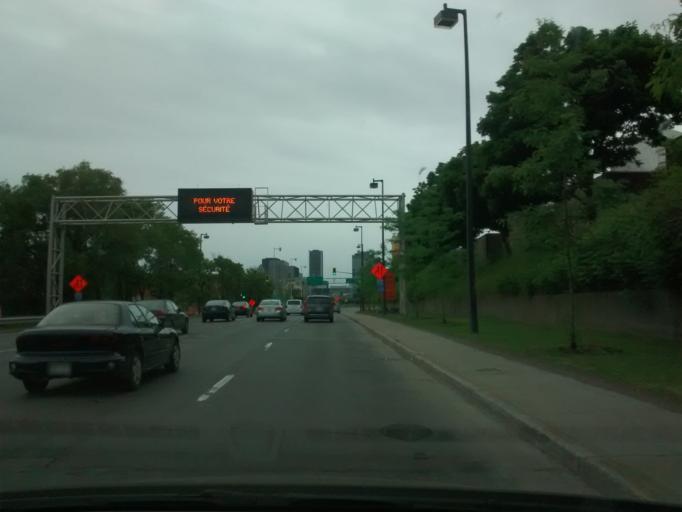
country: CA
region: Quebec
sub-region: Monteregie
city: Longueuil
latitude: 45.5185
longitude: -73.5495
